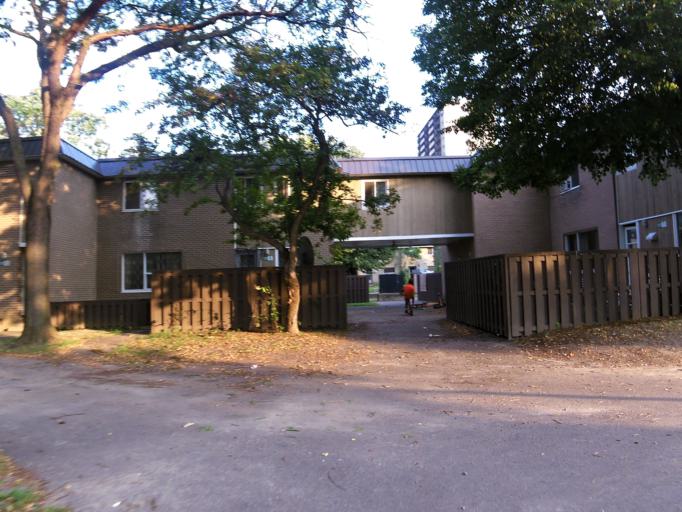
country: CA
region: Ontario
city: Bells Corners
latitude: 45.3589
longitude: -75.7996
